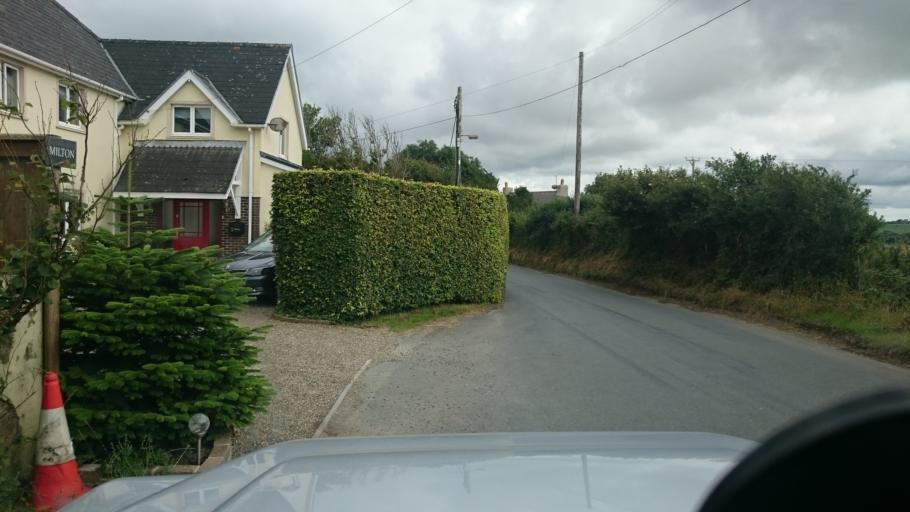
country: GB
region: Wales
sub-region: Pembrokeshire
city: Freystrop
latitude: 51.7638
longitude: -4.9540
